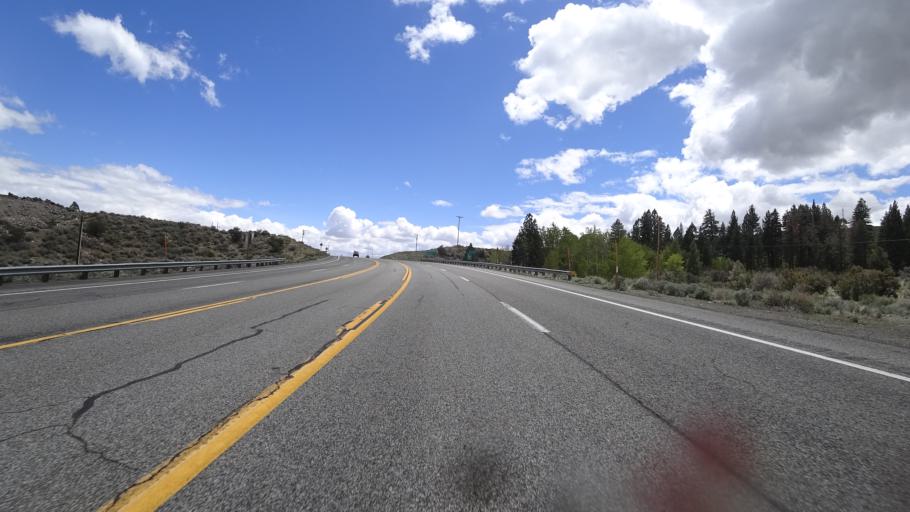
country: US
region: California
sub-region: Mono County
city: Bridgeport
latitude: 37.9511
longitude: -119.1167
